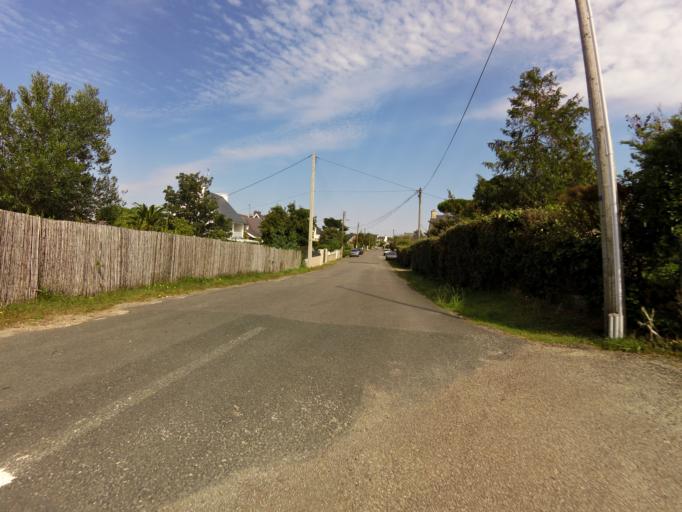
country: FR
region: Brittany
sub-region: Departement du Finistere
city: Loctudy
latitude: 47.8524
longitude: -4.1605
